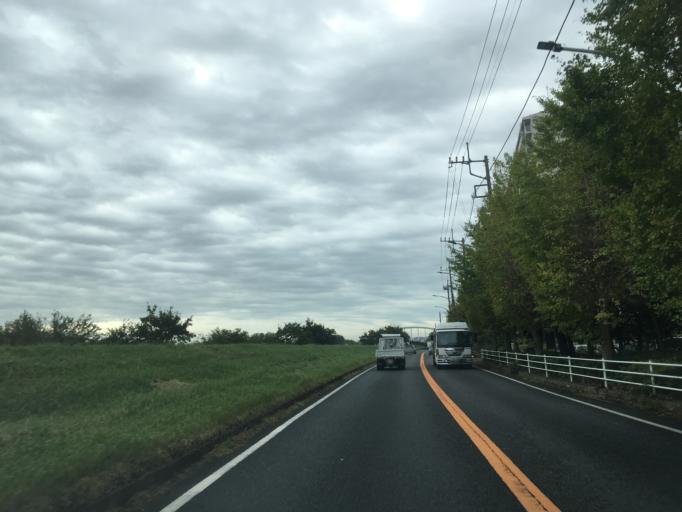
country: JP
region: Tokyo
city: Chofugaoka
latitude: 35.6309
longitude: 139.5624
